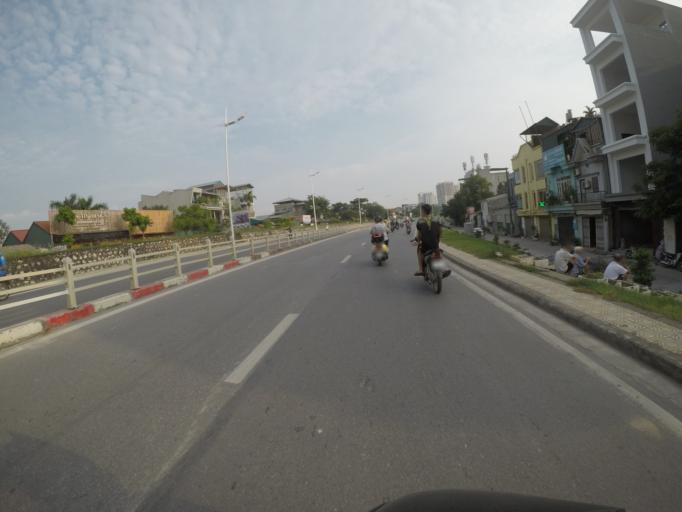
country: VN
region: Ha Noi
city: Tay Ho
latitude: 21.0726
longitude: 105.8257
